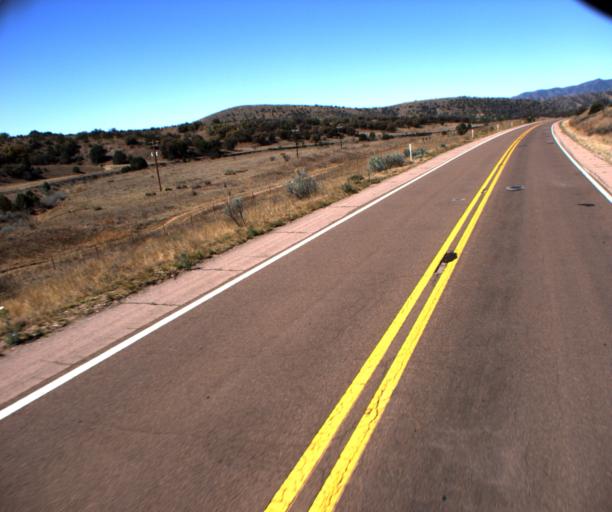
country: US
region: Arizona
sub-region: Pima County
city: Corona de Tucson
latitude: 31.6628
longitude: -110.6838
